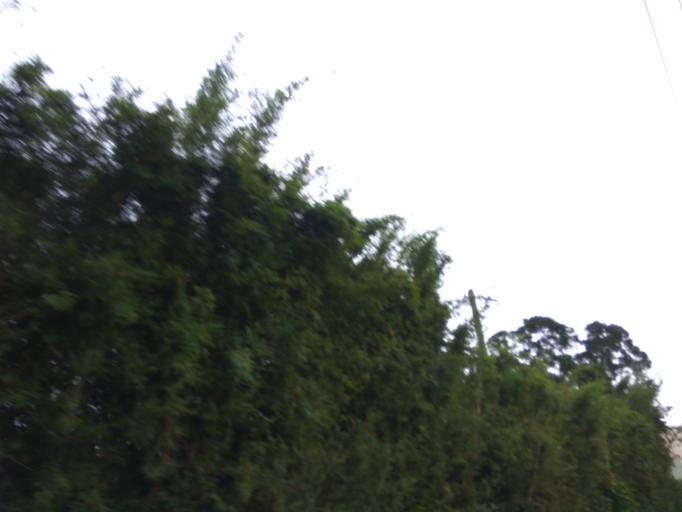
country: TW
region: Taiwan
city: Taoyuan City
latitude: 24.9888
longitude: 121.2280
